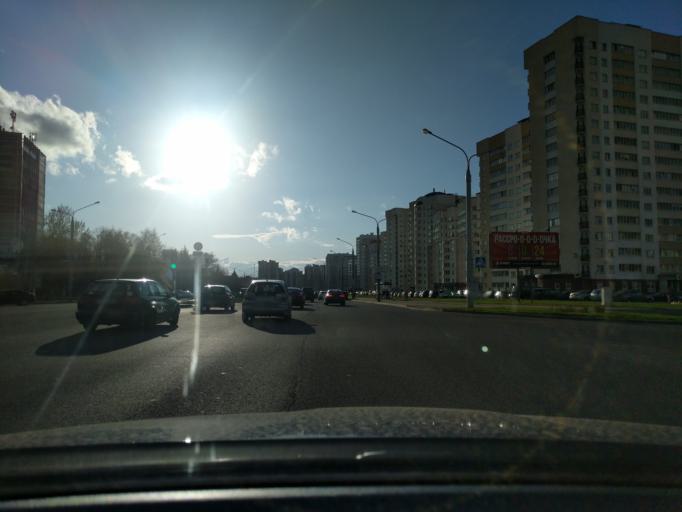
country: BY
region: Minsk
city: Novoye Medvezhino
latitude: 53.9162
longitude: 27.4633
